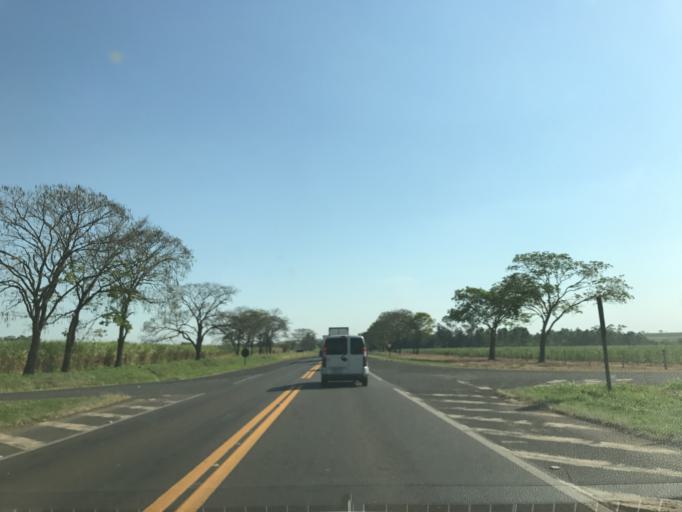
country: BR
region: Sao Paulo
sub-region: Penapolis
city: Penapolis
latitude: -21.4760
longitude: -50.1965
